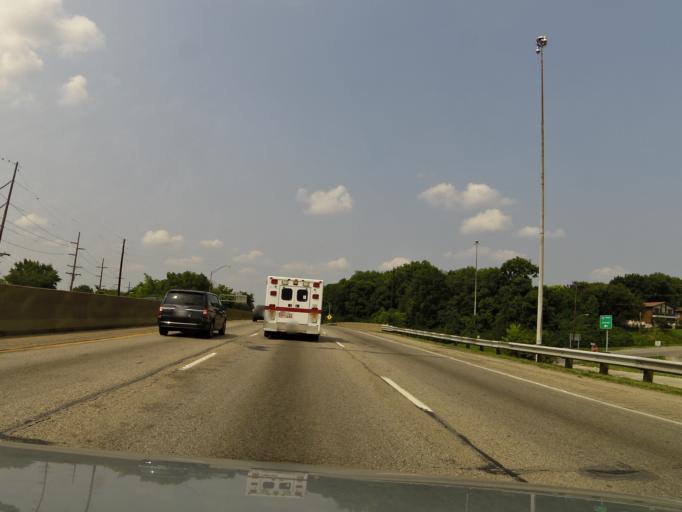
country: US
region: Ohio
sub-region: Hamilton County
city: Elmwood Place
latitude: 39.1830
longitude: -84.4839
